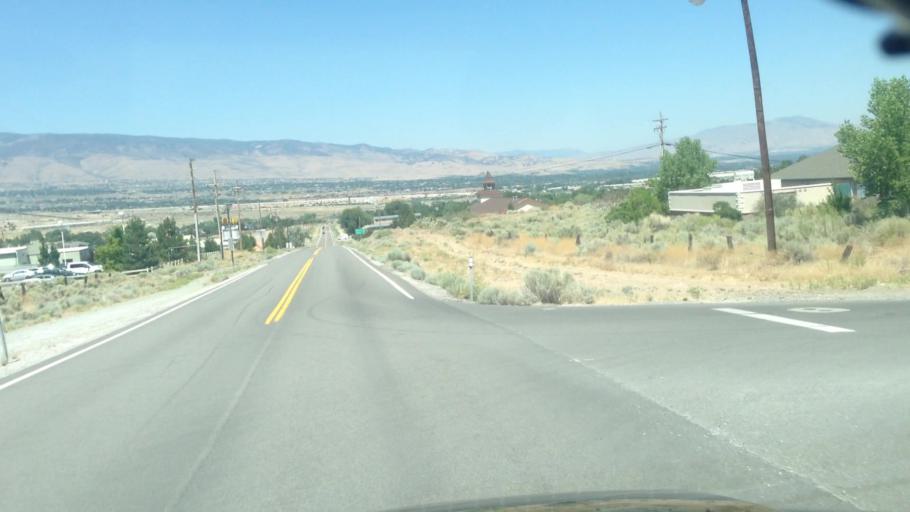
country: US
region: Nevada
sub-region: Storey County
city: Virginia City
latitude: 39.3911
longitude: -119.7185
